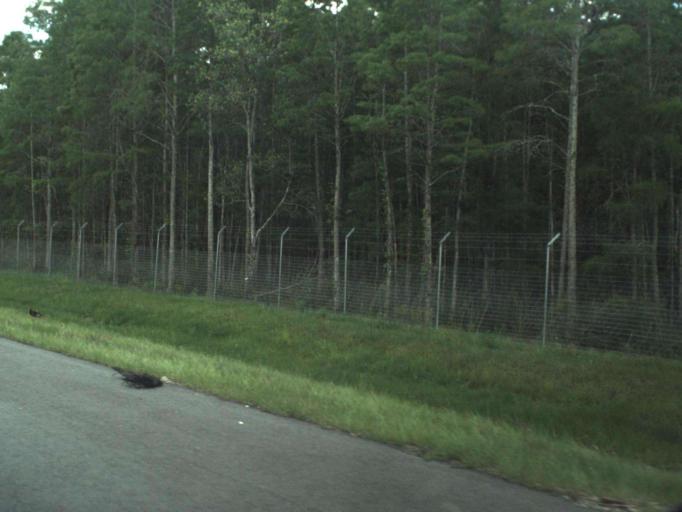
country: US
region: Florida
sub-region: Volusia County
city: Lake Helen
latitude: 29.0376
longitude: -81.2133
